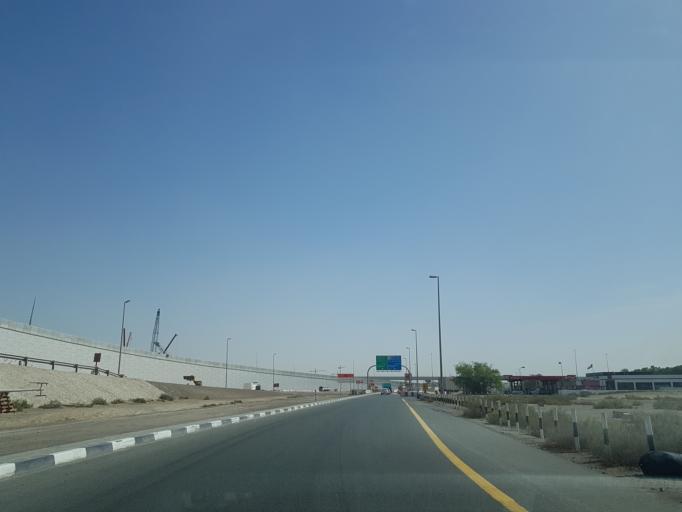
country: AE
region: Dubai
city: Dubai
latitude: 25.0126
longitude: 55.0933
